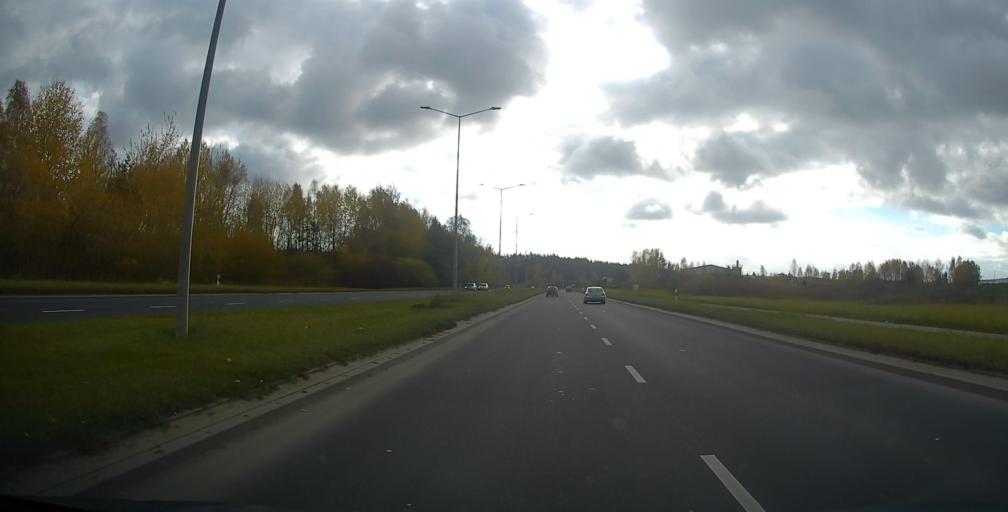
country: PL
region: Warmian-Masurian Voivodeship
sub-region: Powiat elcki
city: Elk
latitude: 53.8225
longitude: 22.3898
